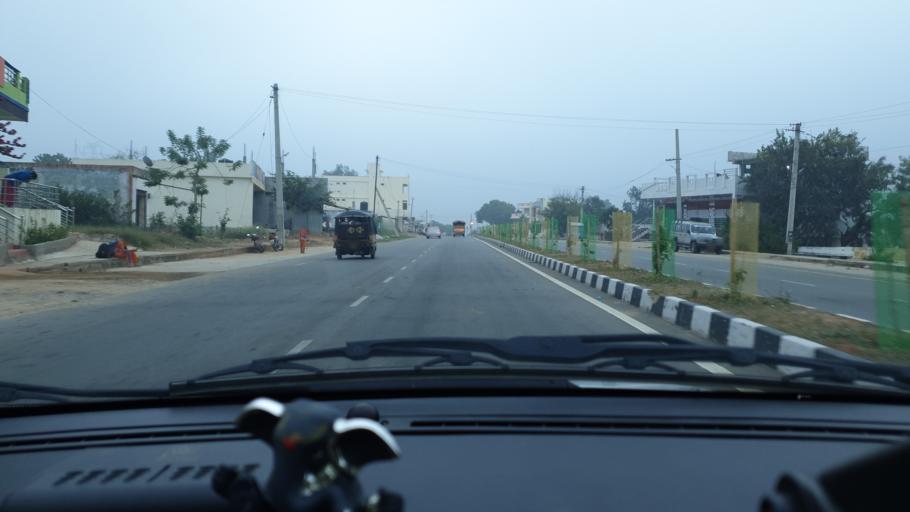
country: IN
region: Telangana
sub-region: Mahbubnagar
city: Farrukhnagar
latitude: 16.9520
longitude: 78.5205
